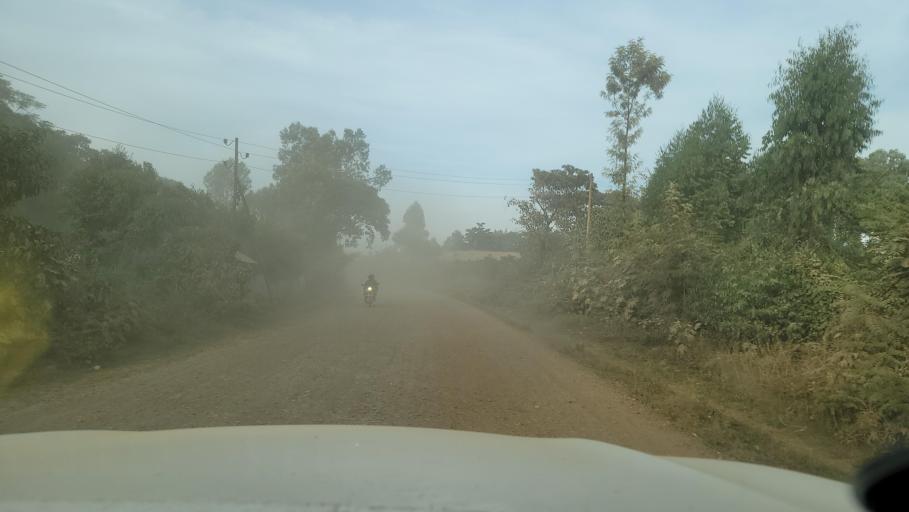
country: ET
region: Oromiya
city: Agaro
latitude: 7.8500
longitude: 36.5670
